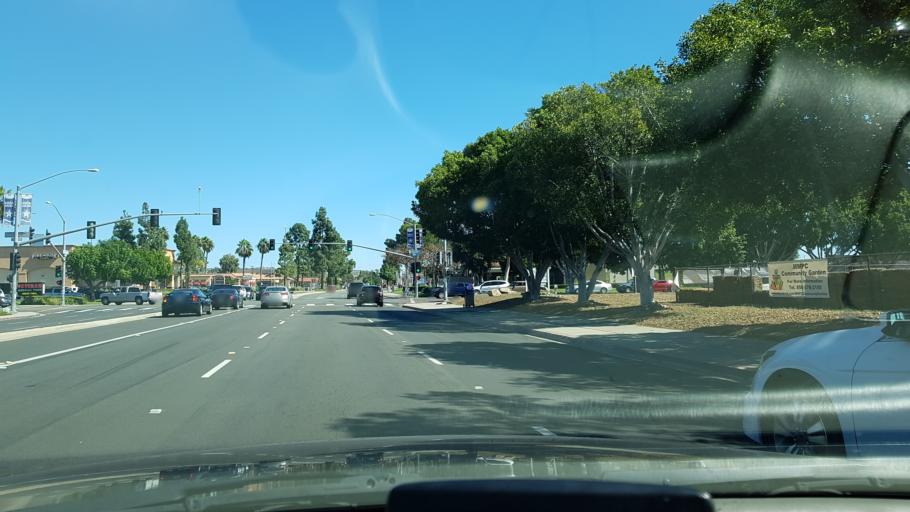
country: US
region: California
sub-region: San Diego County
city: Fairbanks Ranch
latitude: 32.9123
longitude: -117.1500
